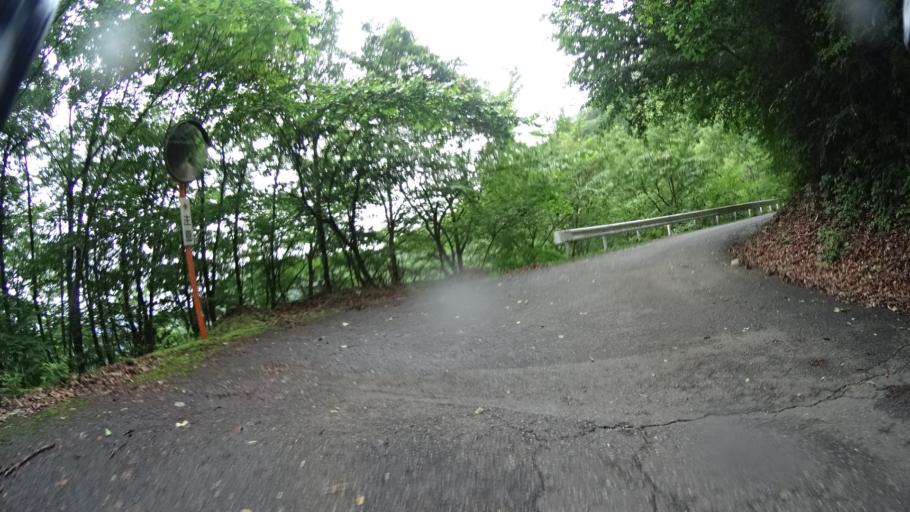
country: JP
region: Saitama
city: Chichibu
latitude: 35.8826
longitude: 139.1132
